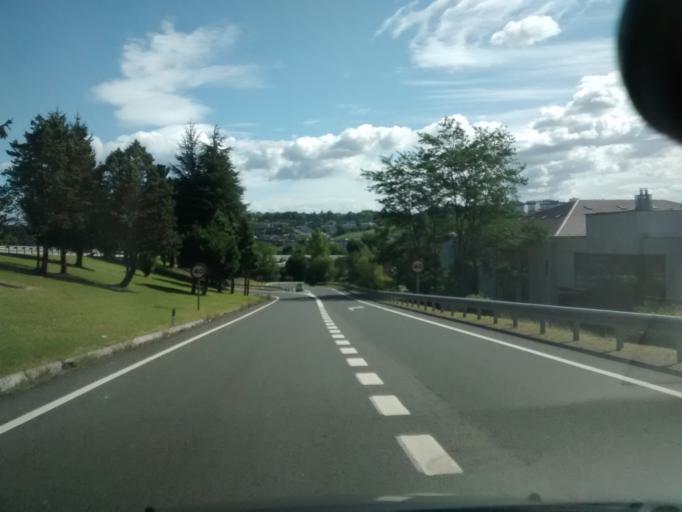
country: ES
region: Basque Country
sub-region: Provincia de Guipuzcoa
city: Lasarte
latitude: 43.2979
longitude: -2.0092
